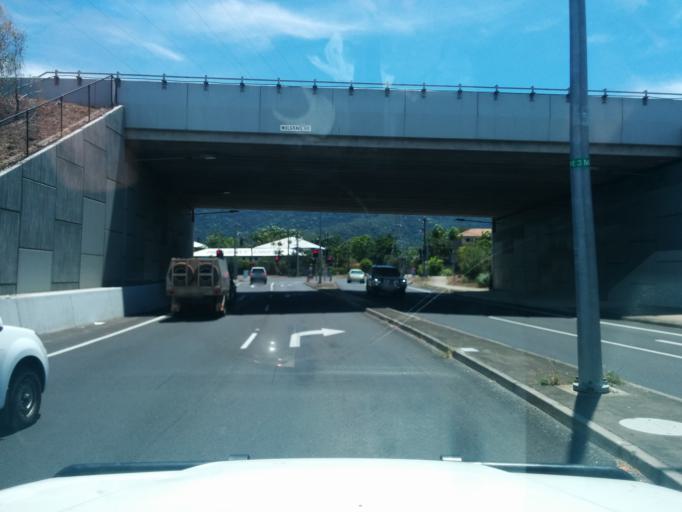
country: AU
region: Queensland
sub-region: Cairns
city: Woree
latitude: -16.9562
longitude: 145.7480
